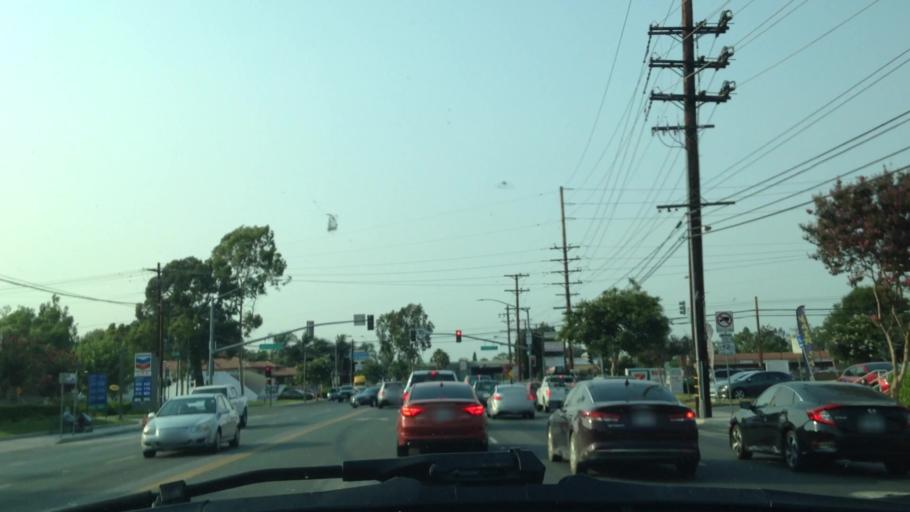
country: US
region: California
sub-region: Orange County
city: Orange
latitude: 33.7725
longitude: -117.8527
